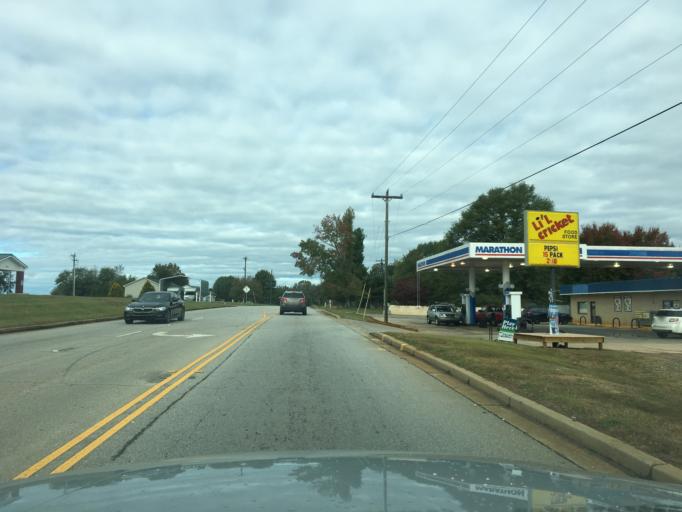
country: US
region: South Carolina
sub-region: Greenville County
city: Greer
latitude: 34.9718
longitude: -82.1999
